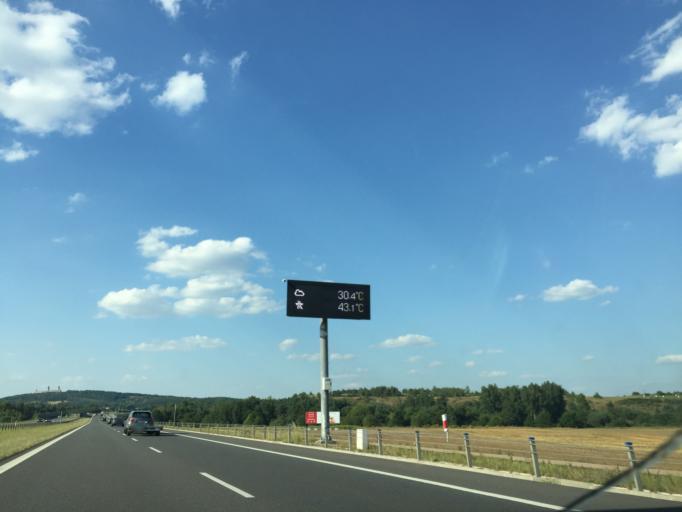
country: PL
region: Swietokrzyskie
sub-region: Powiat kielecki
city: Checiny
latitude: 50.7685
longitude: 20.4642
